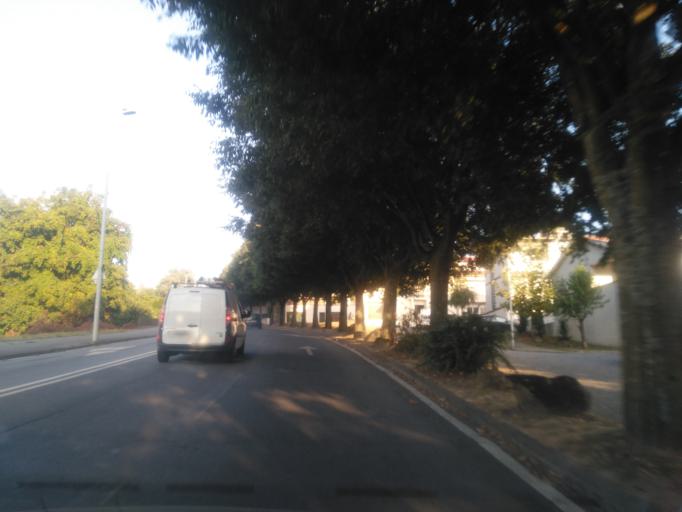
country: PT
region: Braga
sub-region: Braga
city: Braga
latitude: 41.5567
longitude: -8.4404
